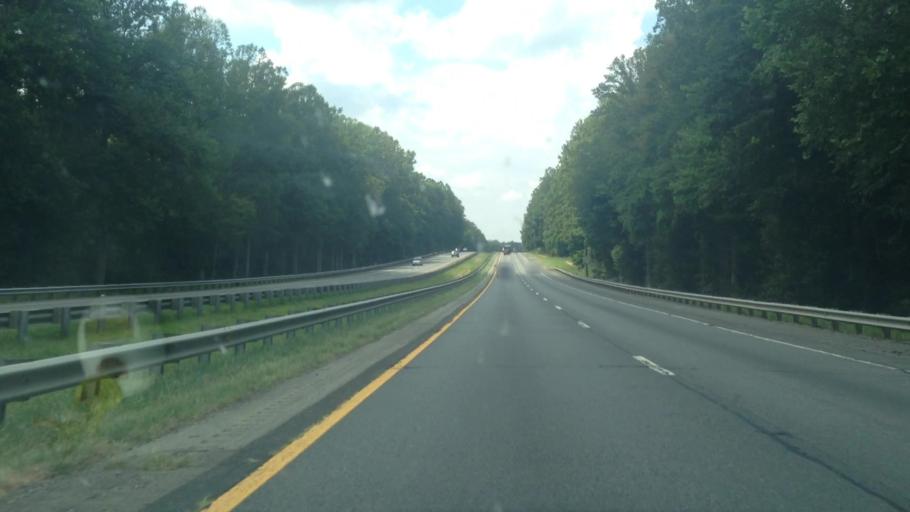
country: US
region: North Carolina
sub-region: Forsyth County
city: Rural Hall
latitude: 36.2325
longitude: -80.3311
